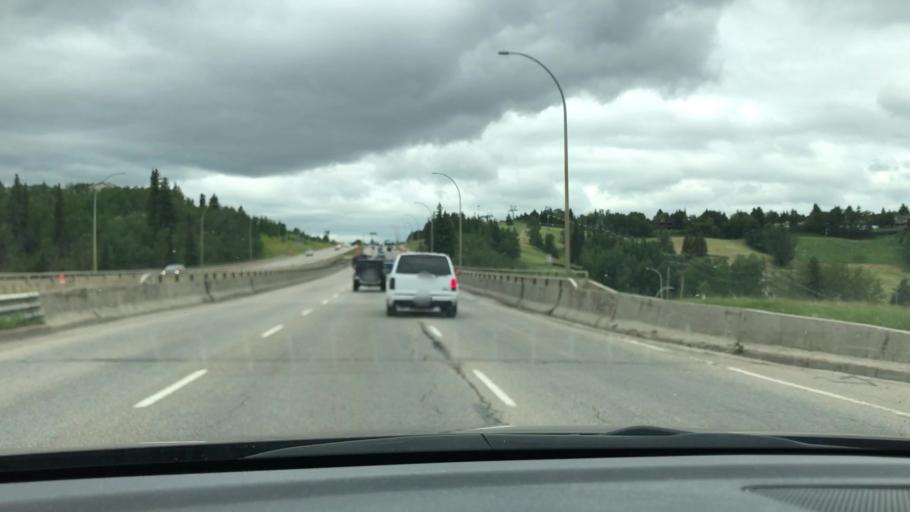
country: CA
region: Alberta
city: Edmonton
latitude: 53.4826
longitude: -113.5529
